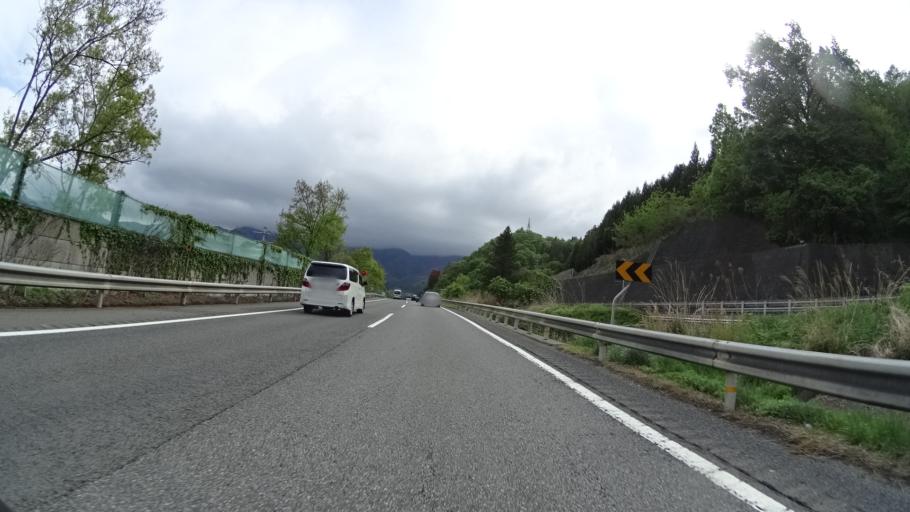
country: JP
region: Nagano
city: Nagano-shi
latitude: 36.5337
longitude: 138.0881
